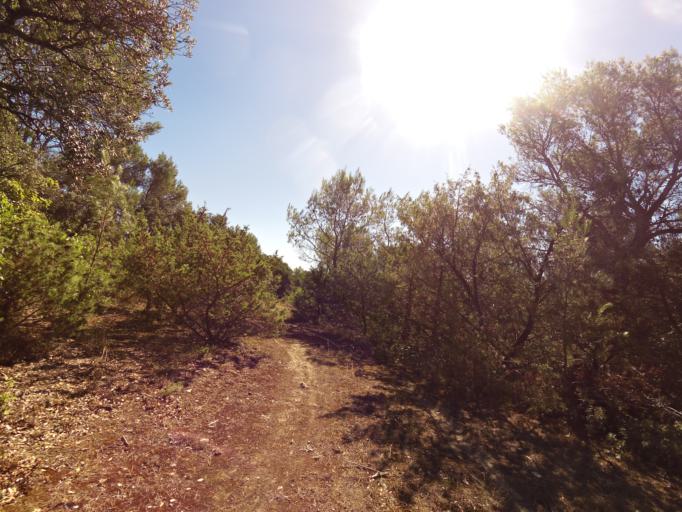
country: FR
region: Languedoc-Roussillon
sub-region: Departement du Gard
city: Congenies
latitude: 43.7616
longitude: 4.1862
